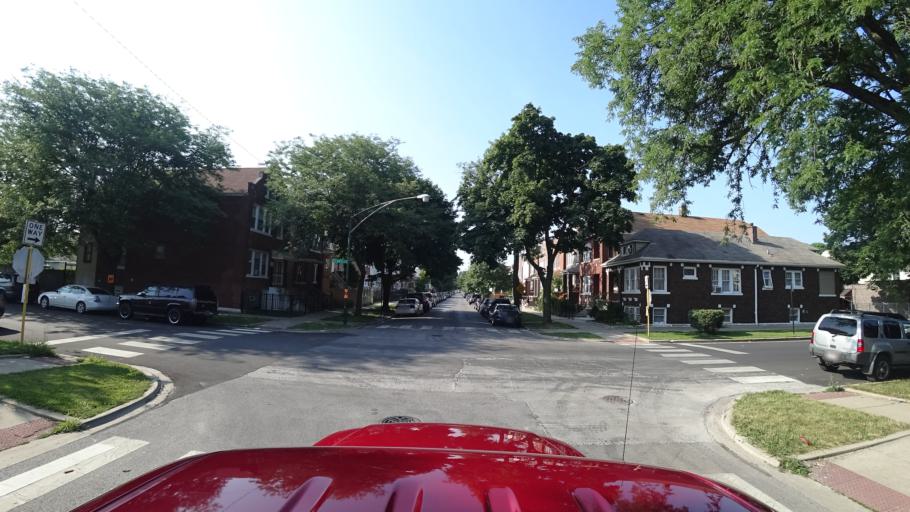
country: US
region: Illinois
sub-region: Cook County
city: Chicago
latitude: 41.8120
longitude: -87.6956
